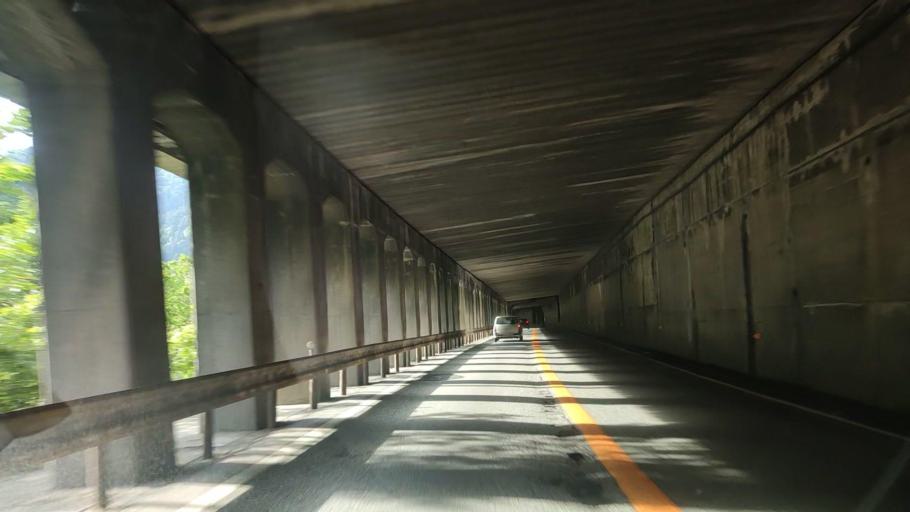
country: JP
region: Toyama
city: Yatsuomachi-higashikumisaka
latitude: 36.4450
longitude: 137.2734
